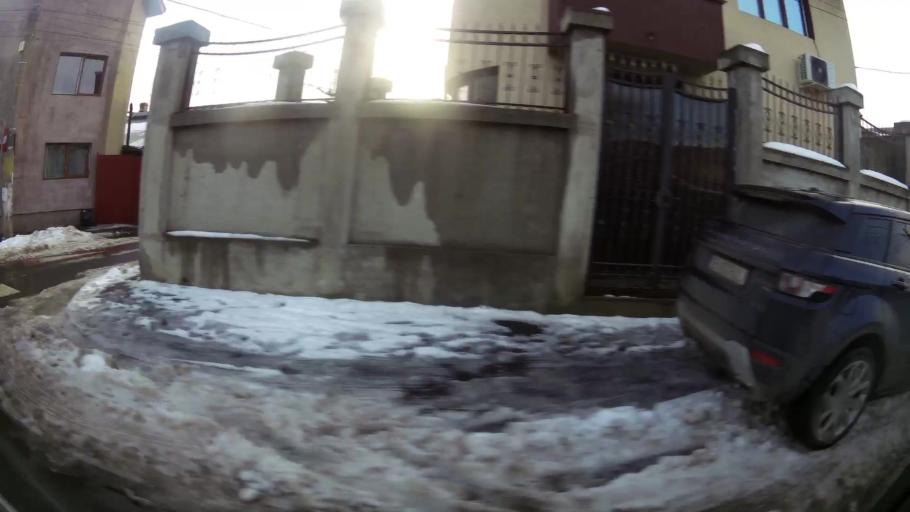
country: RO
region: Bucuresti
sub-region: Municipiul Bucuresti
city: Bucuresti
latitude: 44.3945
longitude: 26.0723
